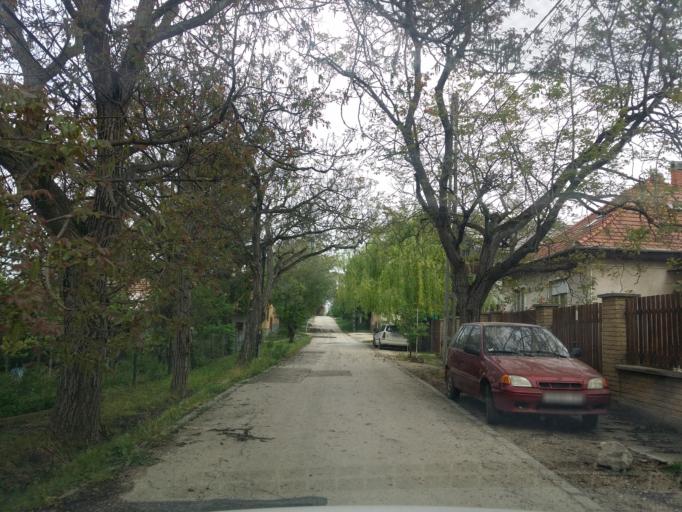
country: HU
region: Pest
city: Biatorbagy
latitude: 47.4742
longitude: 18.8343
